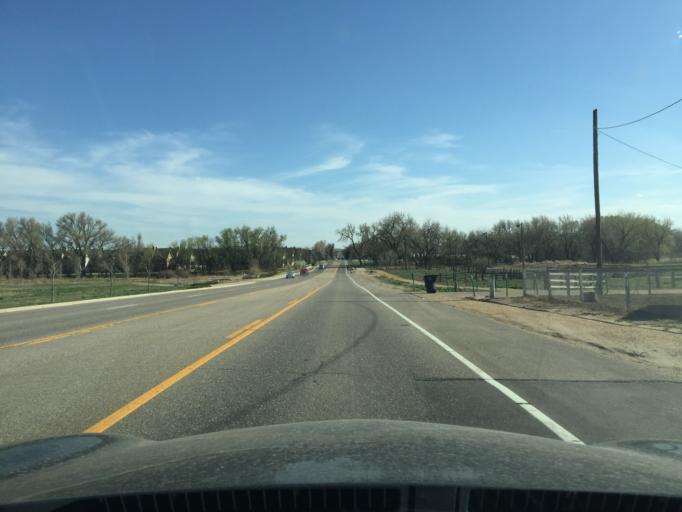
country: US
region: Colorado
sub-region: Boulder County
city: Longmont
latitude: 40.1366
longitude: -105.1309
